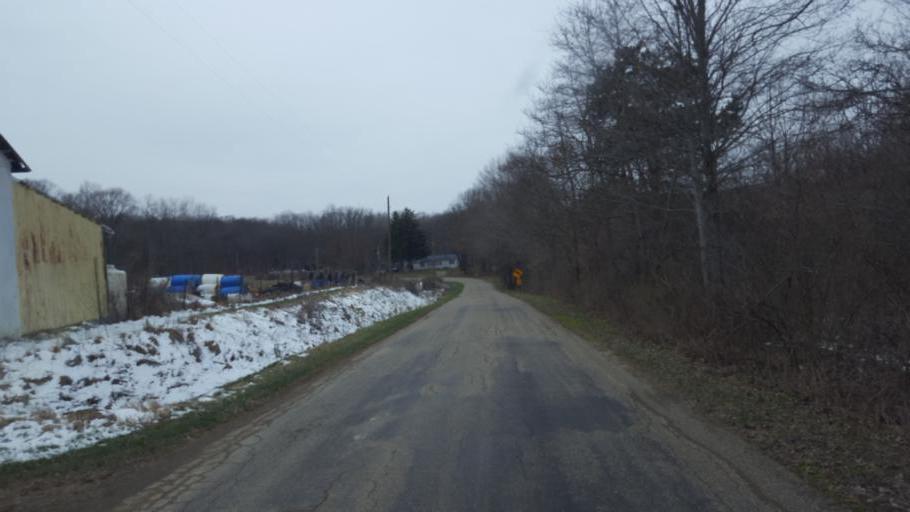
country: US
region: Ohio
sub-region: Sandusky County
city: Bellville
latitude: 40.5869
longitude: -82.4483
